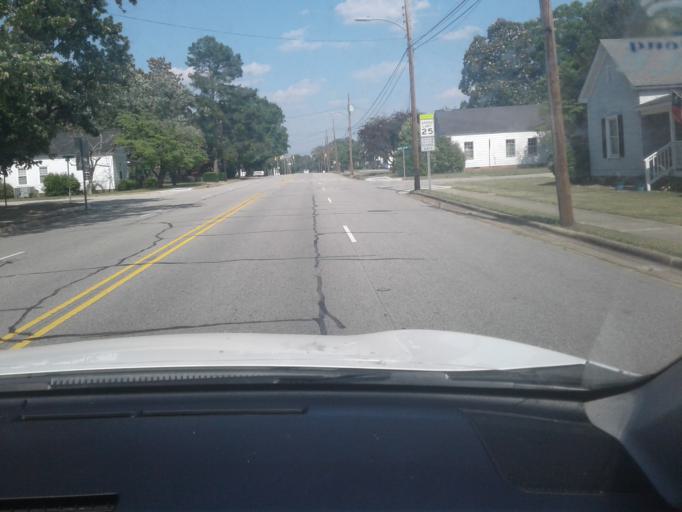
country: US
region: North Carolina
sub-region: Harnett County
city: Erwin
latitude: 35.3269
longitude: -78.6733
